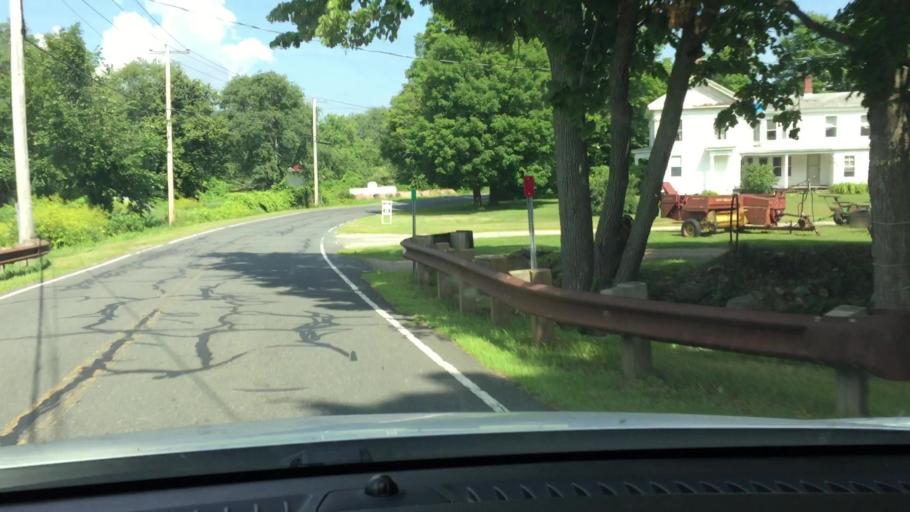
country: US
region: Massachusetts
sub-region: Berkshire County
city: Lee
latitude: 42.2302
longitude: -73.1934
